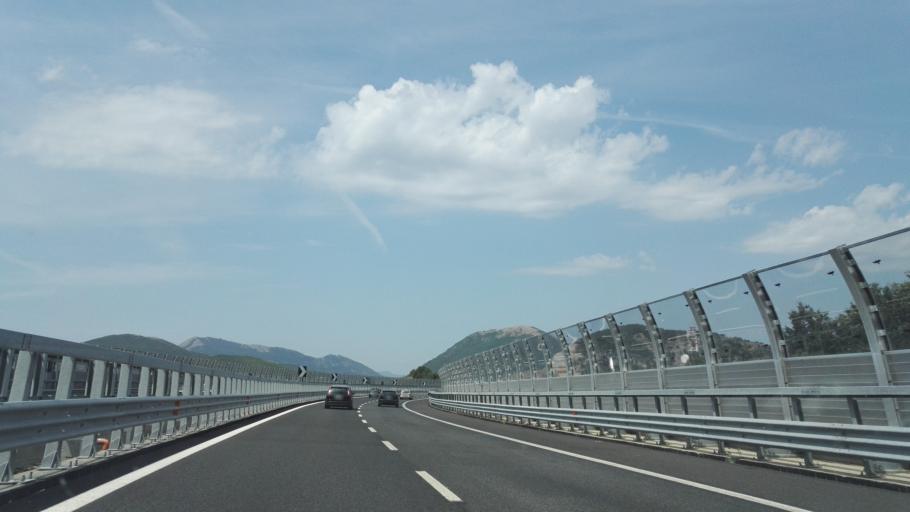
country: IT
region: Basilicate
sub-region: Provincia di Potenza
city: Lagonegro
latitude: 40.1304
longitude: 15.7653
